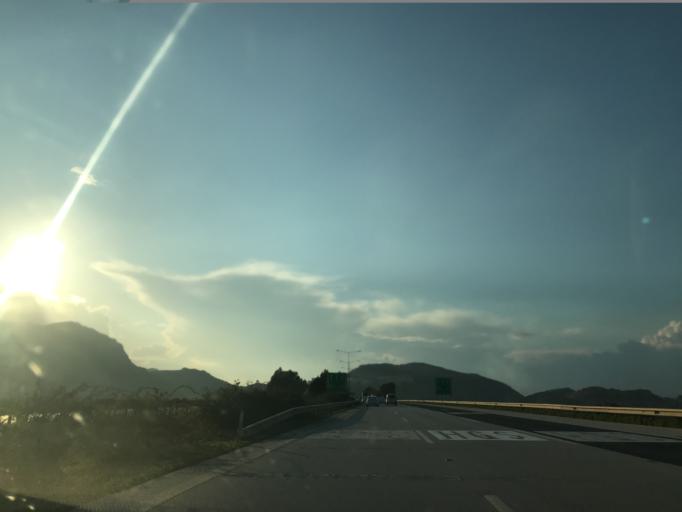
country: TR
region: Adana
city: Ceyhan
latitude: 36.9867
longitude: 35.7631
